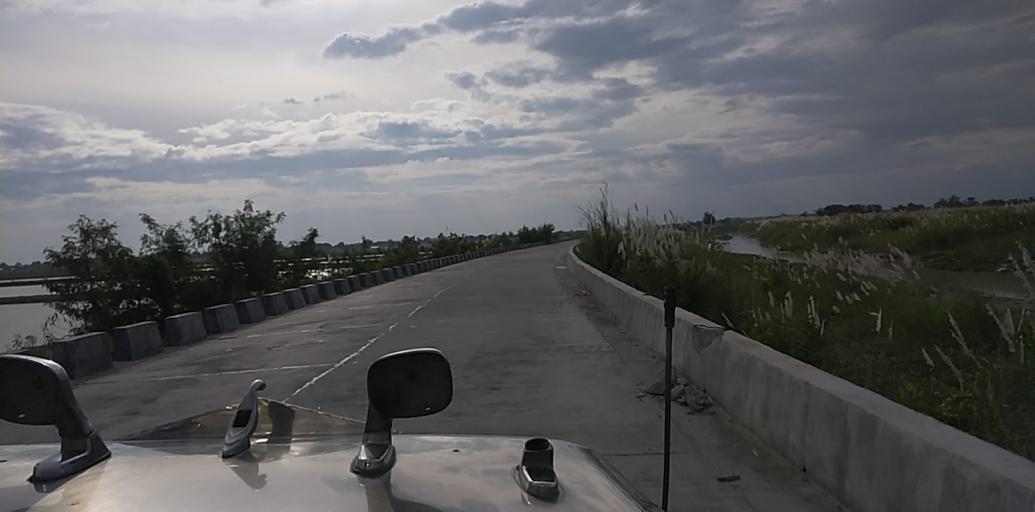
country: PH
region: Central Luzon
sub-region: Province of Pampanga
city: Minalin
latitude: 14.9675
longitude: 120.6726
